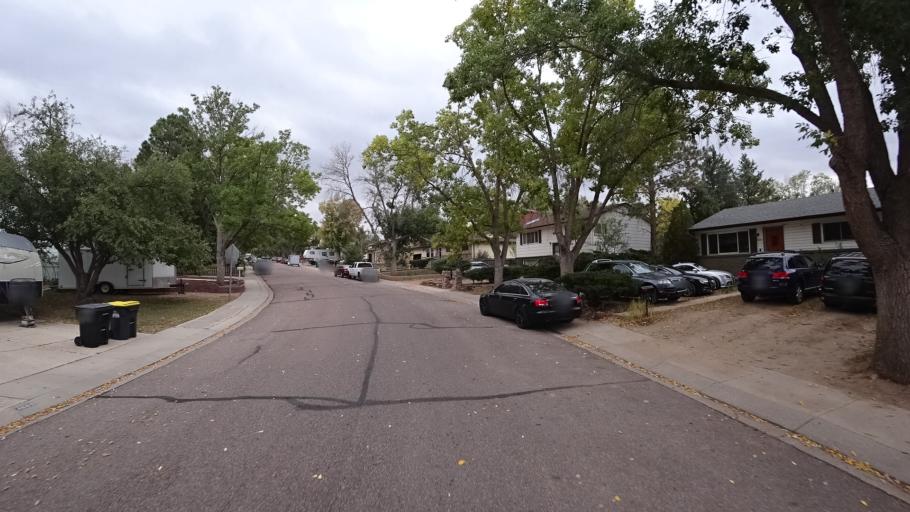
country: US
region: Colorado
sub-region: El Paso County
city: Cimarron Hills
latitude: 38.8897
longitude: -104.7413
